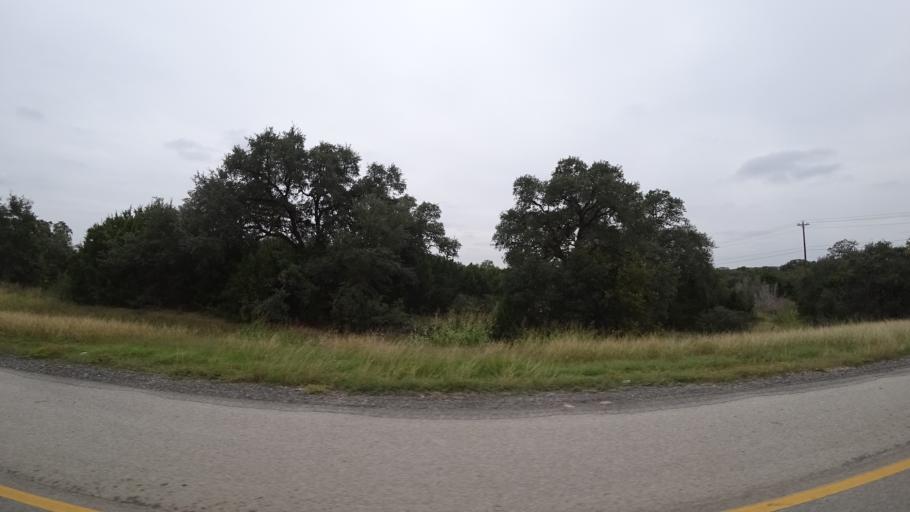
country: US
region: Texas
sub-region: Travis County
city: Shady Hollow
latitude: 30.1833
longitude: -97.9026
